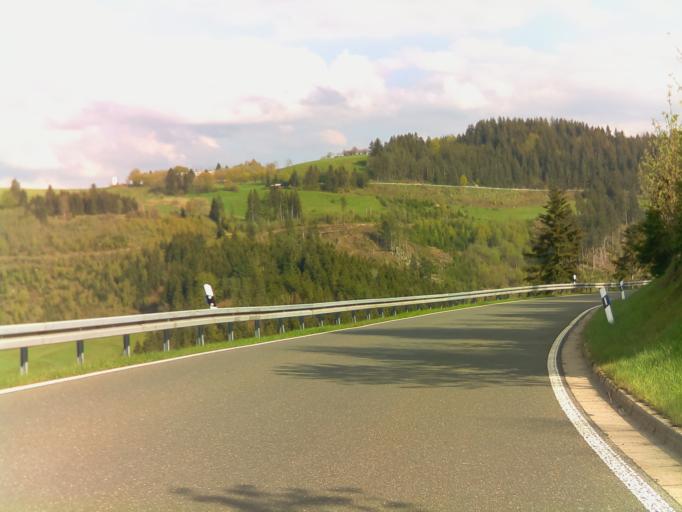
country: DE
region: Thuringia
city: Grafenthal
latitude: 50.5054
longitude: 11.2948
